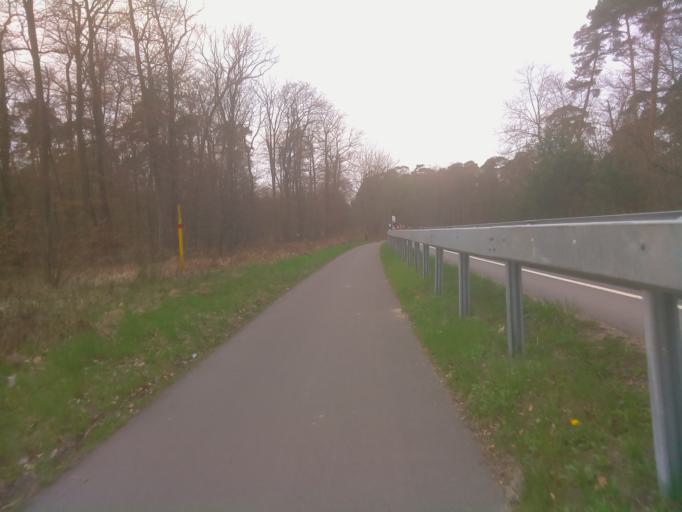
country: DE
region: Hesse
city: Lampertheim
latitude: 49.5965
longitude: 8.5335
